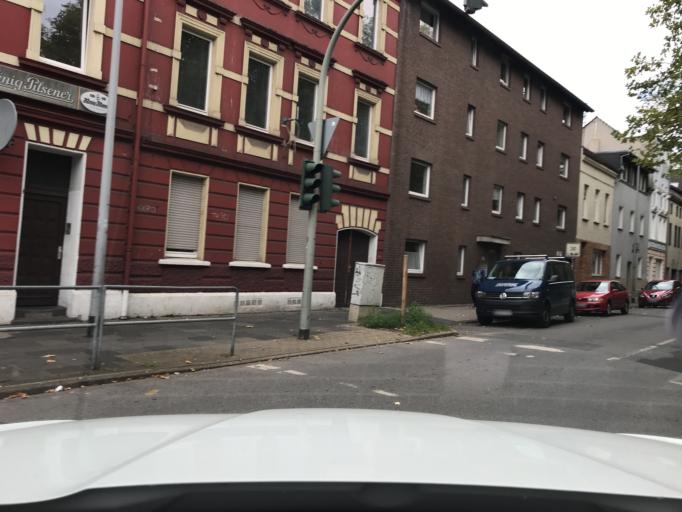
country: DE
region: North Rhine-Westphalia
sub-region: Regierungsbezirk Dusseldorf
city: Hochfeld
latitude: 51.4237
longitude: 6.7592
